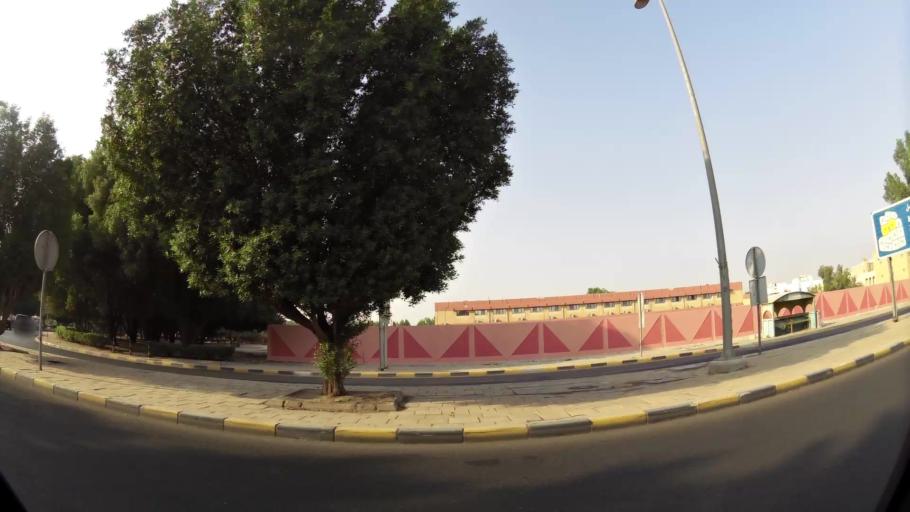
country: KW
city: Bayan
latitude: 29.2984
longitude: 48.0508
